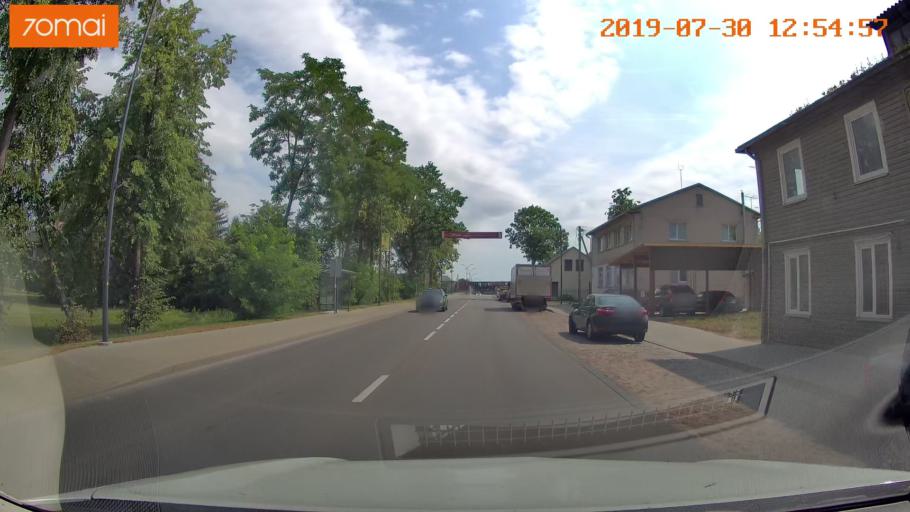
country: LT
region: Marijampoles apskritis
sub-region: Marijampole Municipality
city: Marijampole
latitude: 54.5559
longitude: 23.3578
